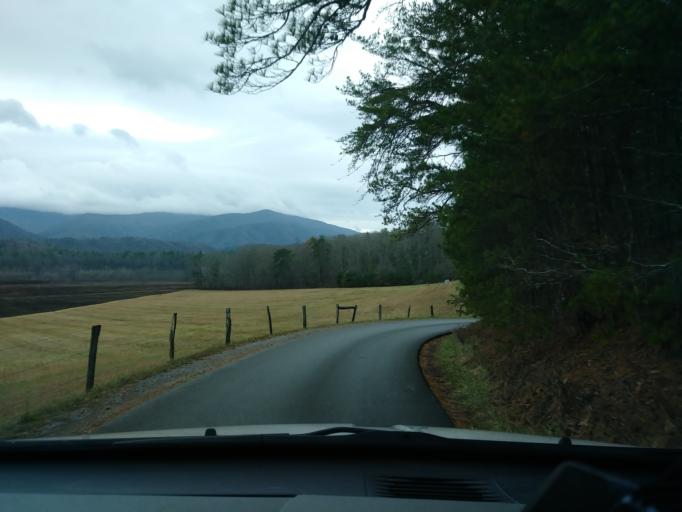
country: US
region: Tennessee
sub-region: Blount County
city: Wildwood
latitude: 35.6033
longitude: -83.8349
